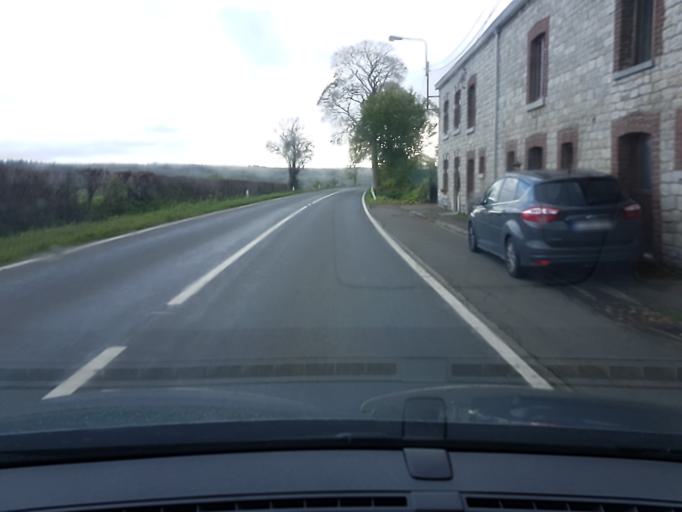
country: BE
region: Wallonia
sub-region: Province de Liege
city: Trooz
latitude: 50.5177
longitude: 5.7288
